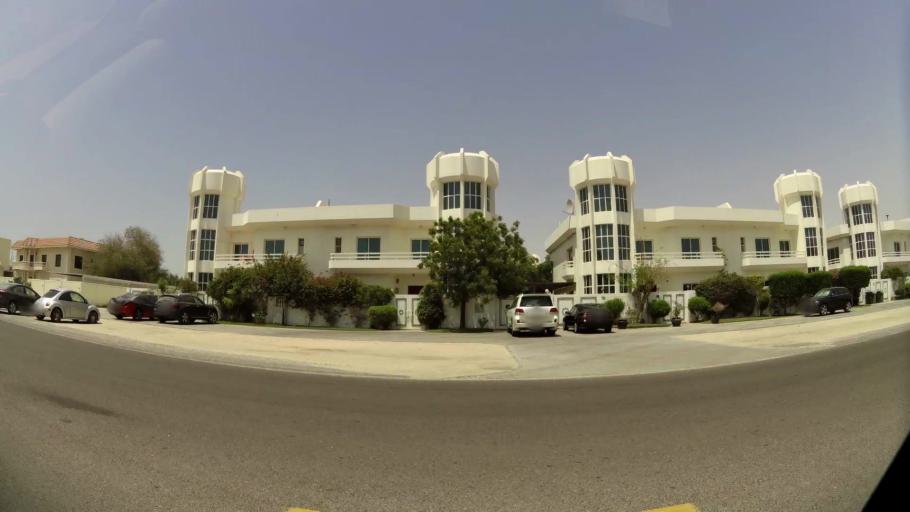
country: AE
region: Dubai
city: Dubai
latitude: 25.1428
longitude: 55.2006
